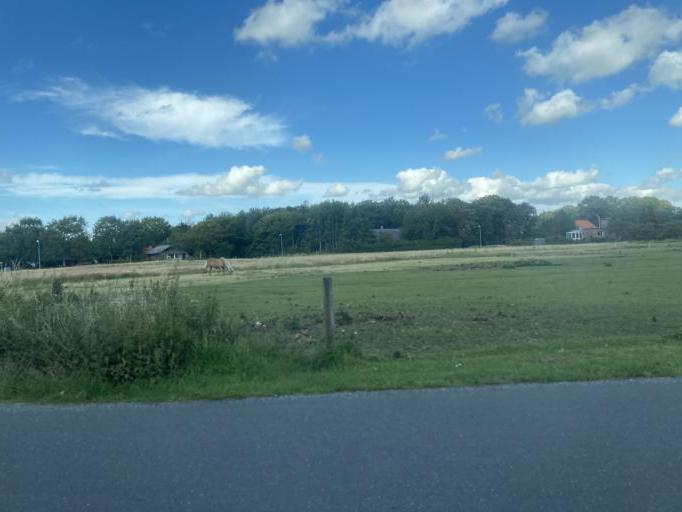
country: DK
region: South Denmark
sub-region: Esbjerg Kommune
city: Ribe
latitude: 55.2905
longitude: 8.6756
